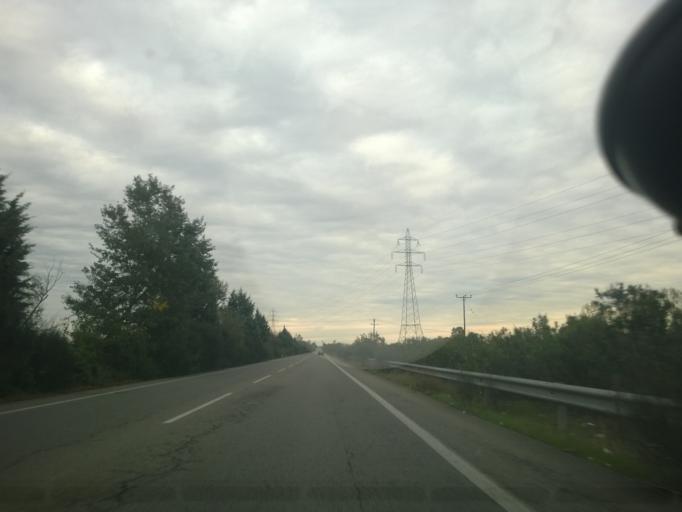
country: GR
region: Central Macedonia
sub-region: Nomos Pellis
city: Melissi
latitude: 40.7779
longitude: 22.3469
